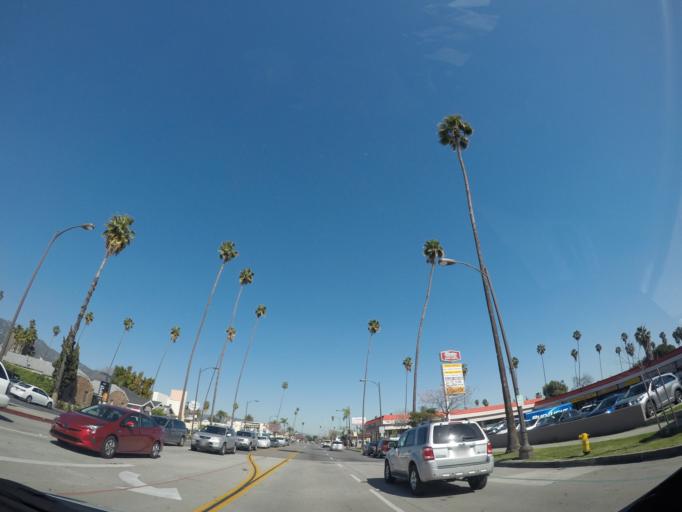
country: US
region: California
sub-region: Los Angeles County
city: East Pasadena
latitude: 34.1460
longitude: -118.1129
